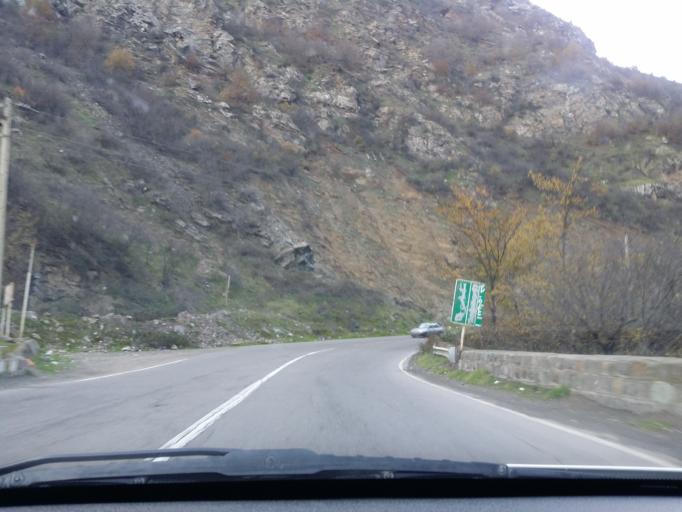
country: IR
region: Mazandaran
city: Chalus
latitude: 36.3051
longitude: 51.2478
